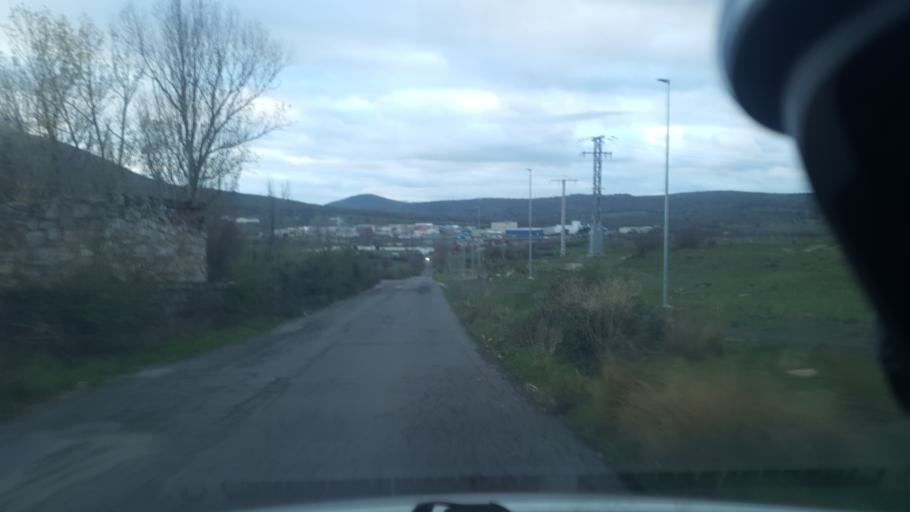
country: ES
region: Castille and Leon
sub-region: Provincia de Segovia
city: Vegas de Matute
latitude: 40.7228
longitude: -4.2500
